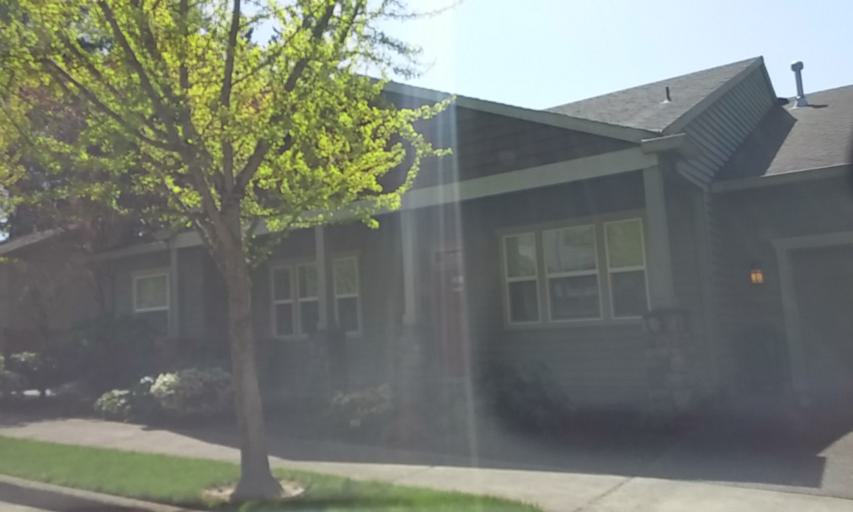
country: US
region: Oregon
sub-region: Washington County
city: West Haven
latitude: 45.5150
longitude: -122.7732
